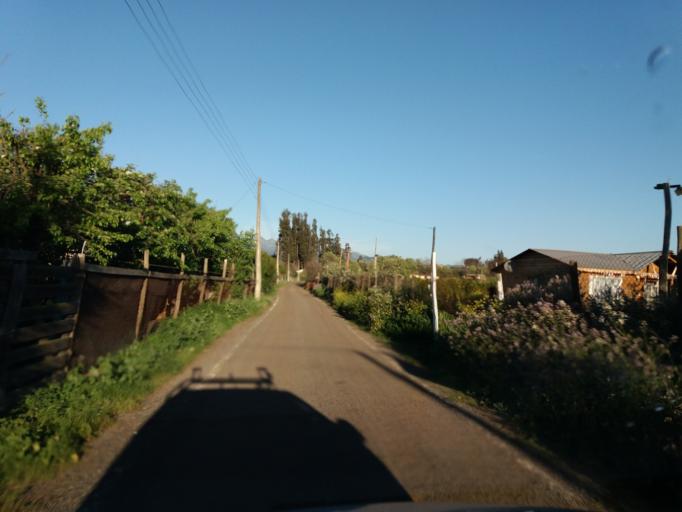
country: CL
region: Valparaiso
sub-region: Provincia de Quillota
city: Quillota
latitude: -32.9131
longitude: -71.3405
